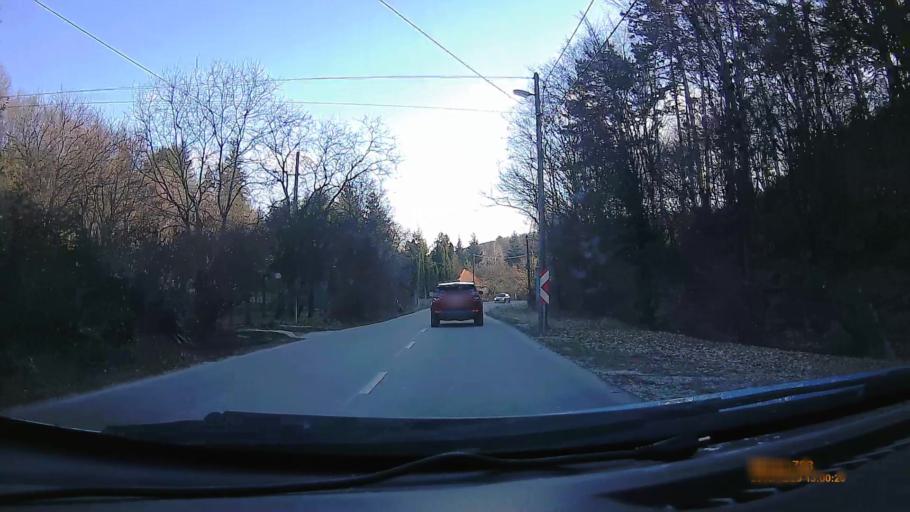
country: HU
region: Heves
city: Abasar
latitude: 47.8180
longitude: 19.9833
